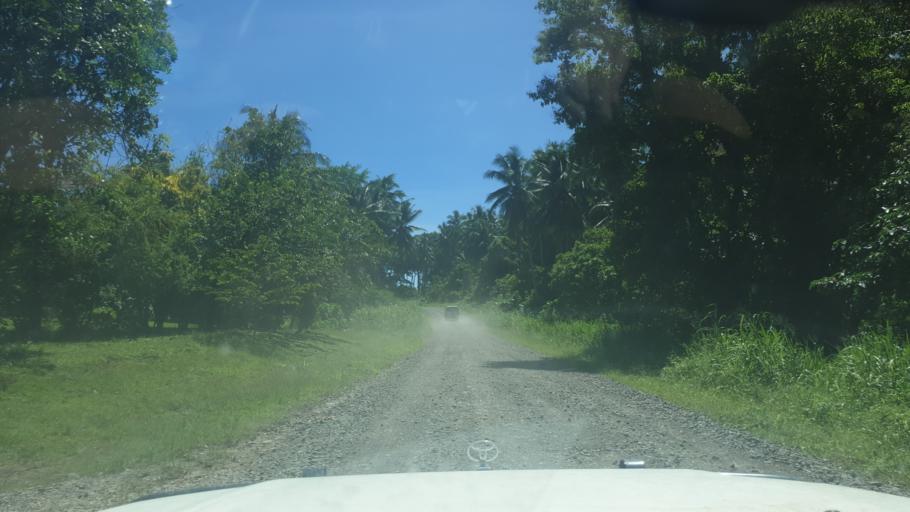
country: PG
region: Bougainville
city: Buka
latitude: -5.6679
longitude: 155.1012
